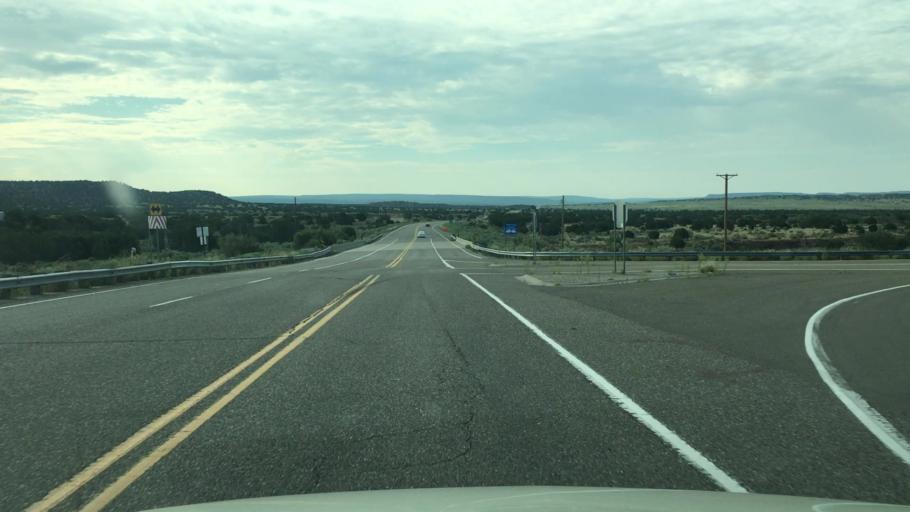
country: US
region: New Mexico
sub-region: Santa Fe County
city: Eldorado at Santa Fe
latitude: 35.4637
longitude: -105.8987
